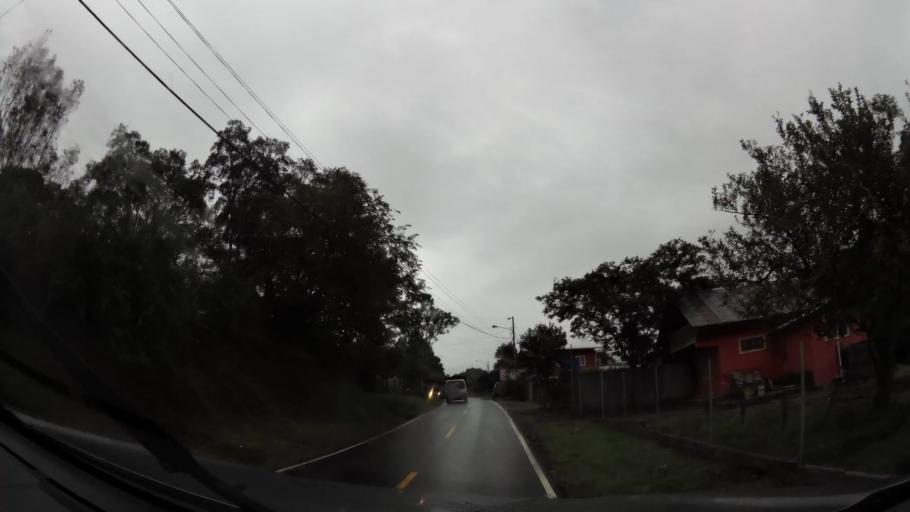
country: PA
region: Chiriqui
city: Volcan
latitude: 8.7919
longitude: -82.6503
